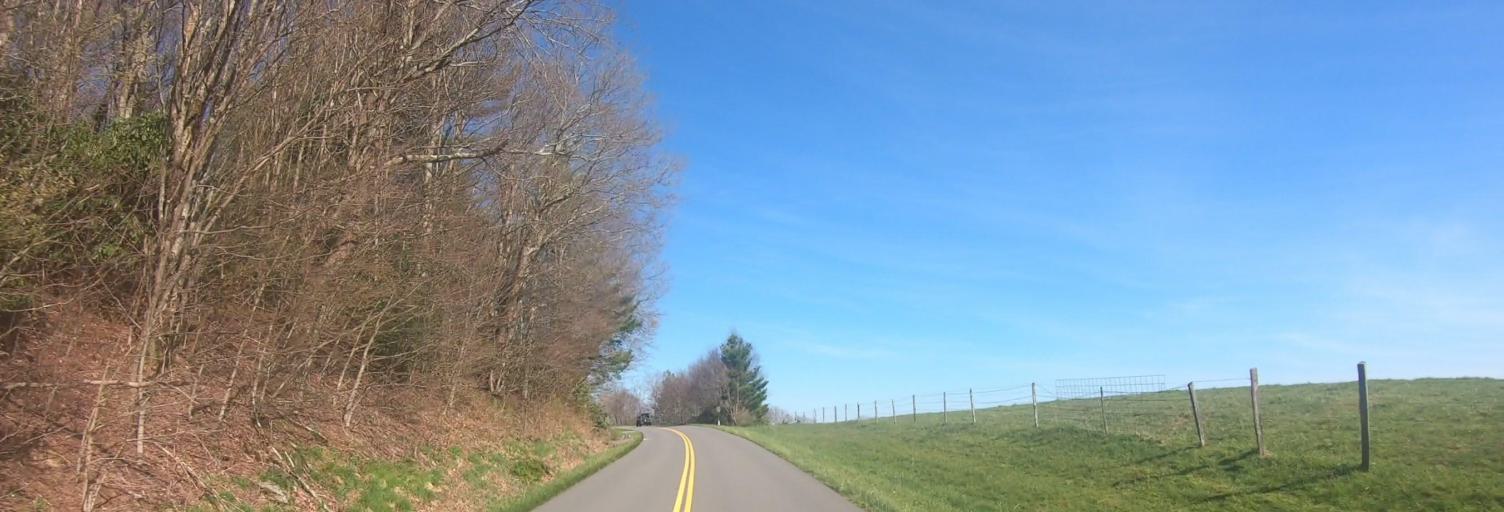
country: US
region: North Carolina
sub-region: Watauga County
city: Blowing Rock
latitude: 36.1368
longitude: -81.6481
